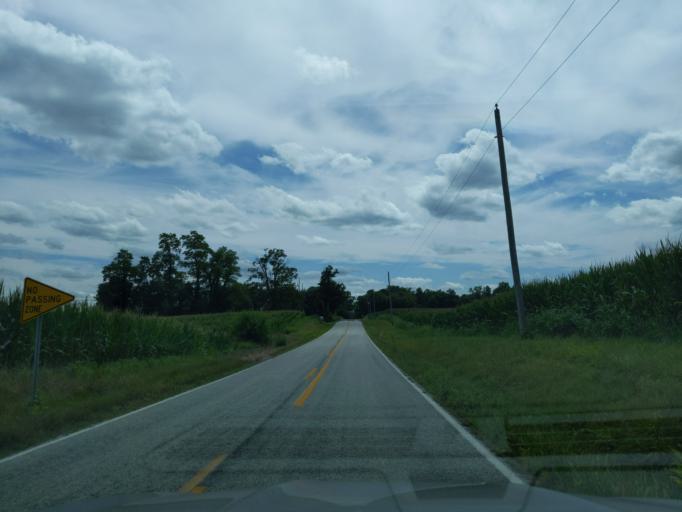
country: US
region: Indiana
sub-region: Ripley County
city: Osgood
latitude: 39.2018
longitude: -85.2776
